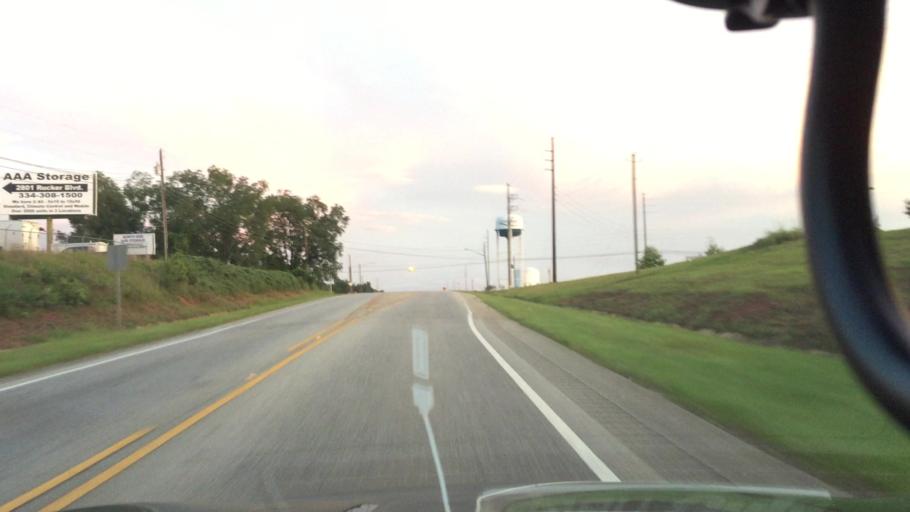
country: US
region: Alabama
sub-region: Coffee County
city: Enterprise
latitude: 31.3623
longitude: -85.8675
